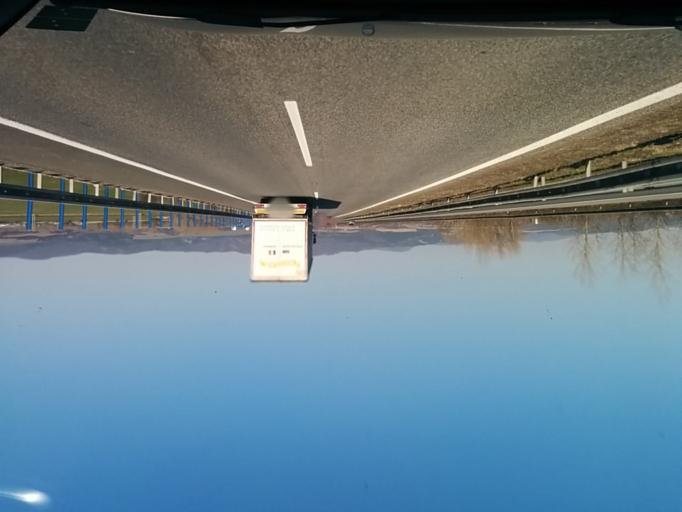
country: SK
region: Trnavsky
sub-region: Okres Trnava
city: Piestany
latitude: 48.6479
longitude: 17.8293
